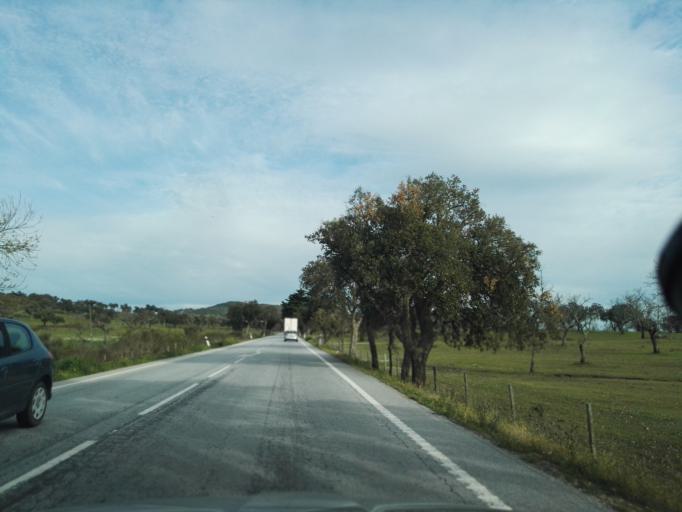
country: PT
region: Portalegre
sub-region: Portalegre
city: Fortios
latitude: 39.3357
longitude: -7.5186
